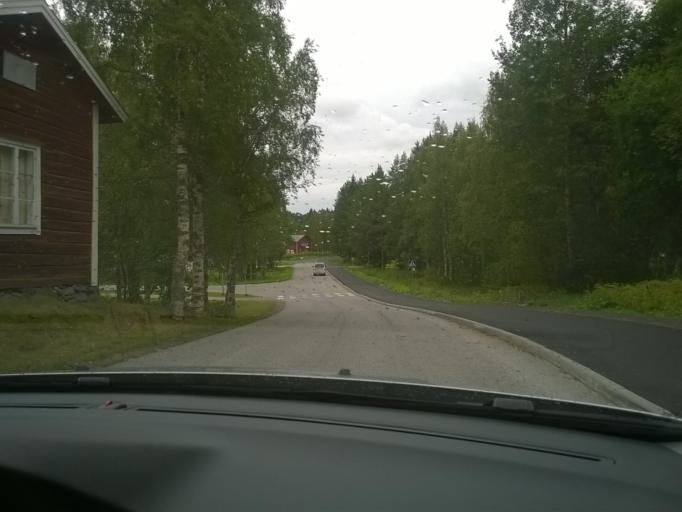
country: FI
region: Kainuu
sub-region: Kehys-Kainuu
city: Kuhmo
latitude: 64.1249
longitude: 29.5032
